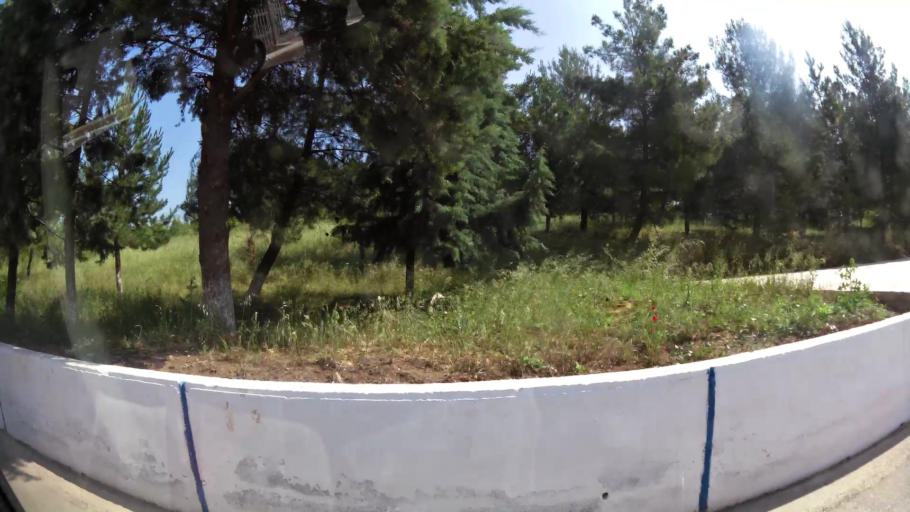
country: GR
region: West Macedonia
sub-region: Nomos Kozanis
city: Koila
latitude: 40.3377
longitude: 21.7891
